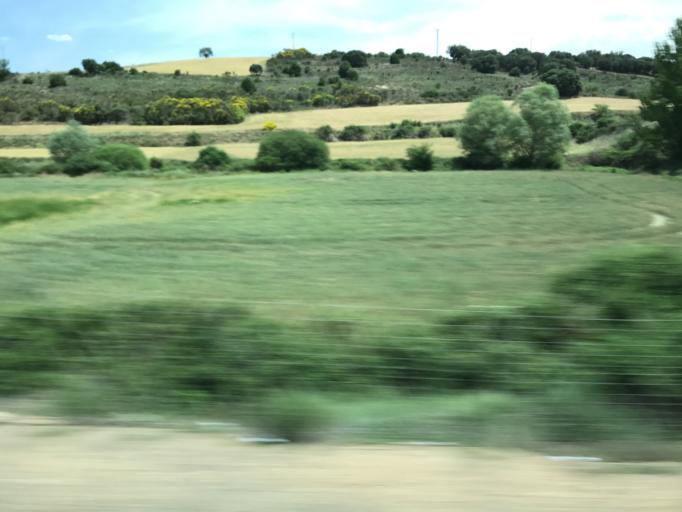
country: ES
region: Castille and Leon
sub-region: Provincia de Burgos
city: Villalmanzo
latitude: 42.0578
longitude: -3.7421
